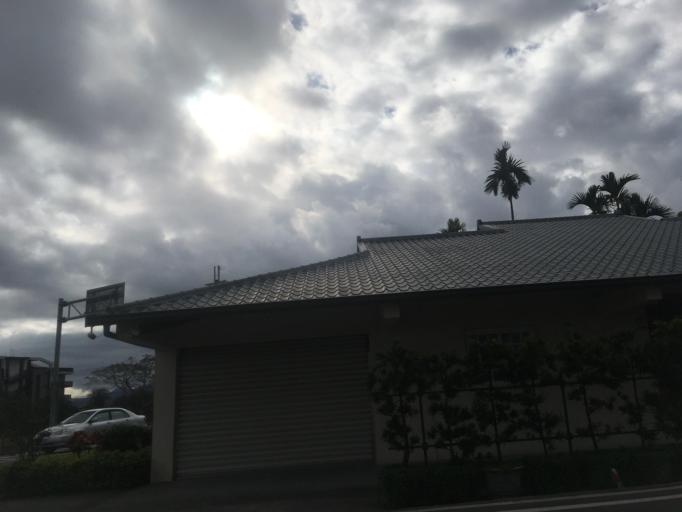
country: TW
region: Taiwan
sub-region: Yilan
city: Yilan
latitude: 24.6814
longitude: 121.6888
